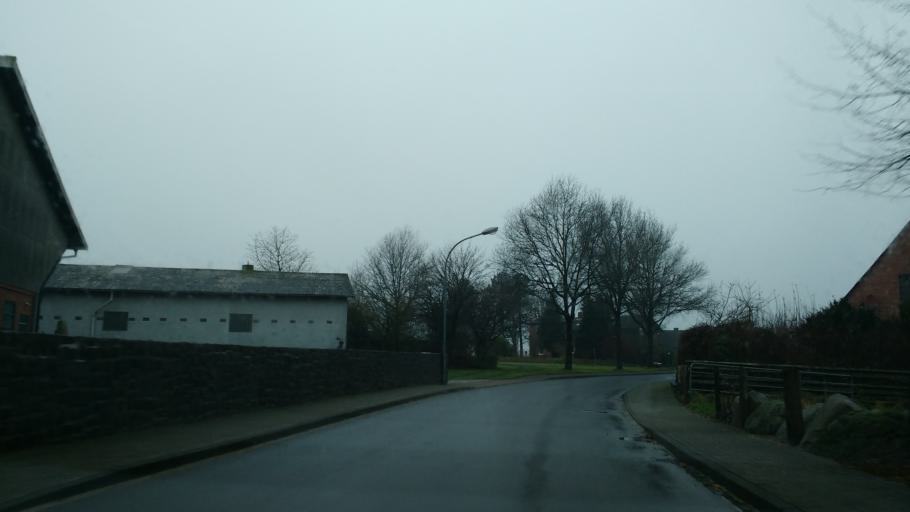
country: DE
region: Schleswig-Holstein
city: Nindorf
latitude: 54.1330
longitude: 9.6920
